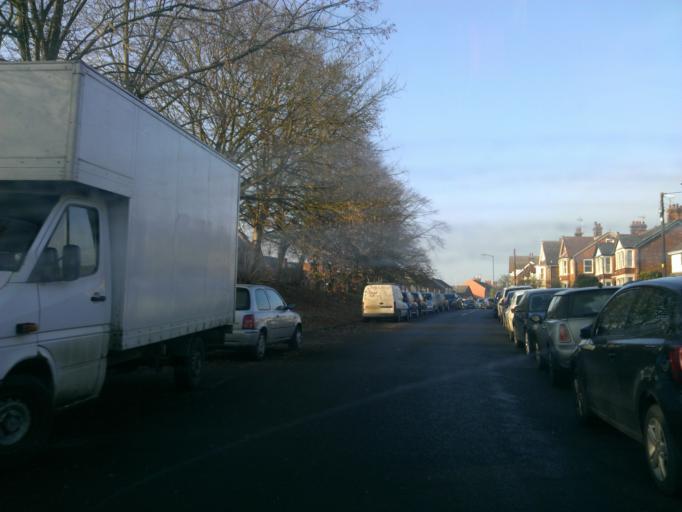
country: GB
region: England
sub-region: Essex
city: Great Dunmow
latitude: 51.8683
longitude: 0.3668
